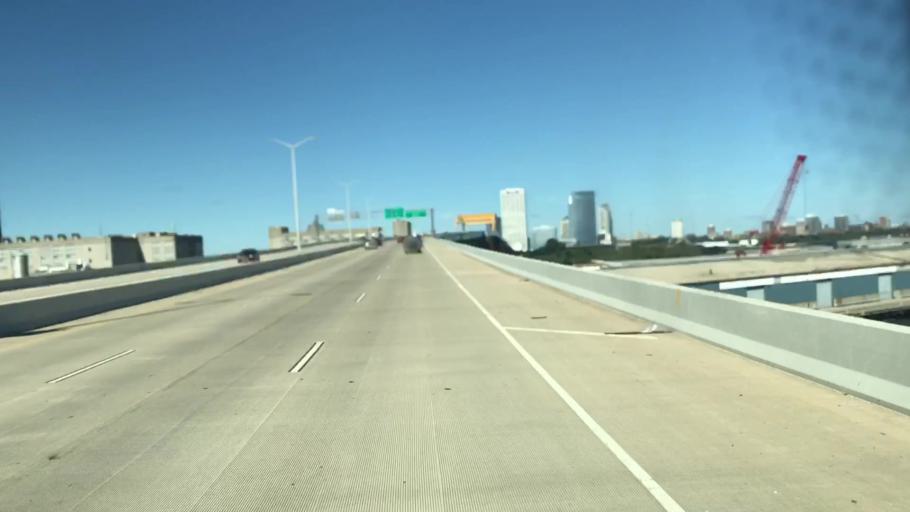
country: US
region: Wisconsin
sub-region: Milwaukee County
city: Milwaukee
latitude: 43.0175
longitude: -87.8963
